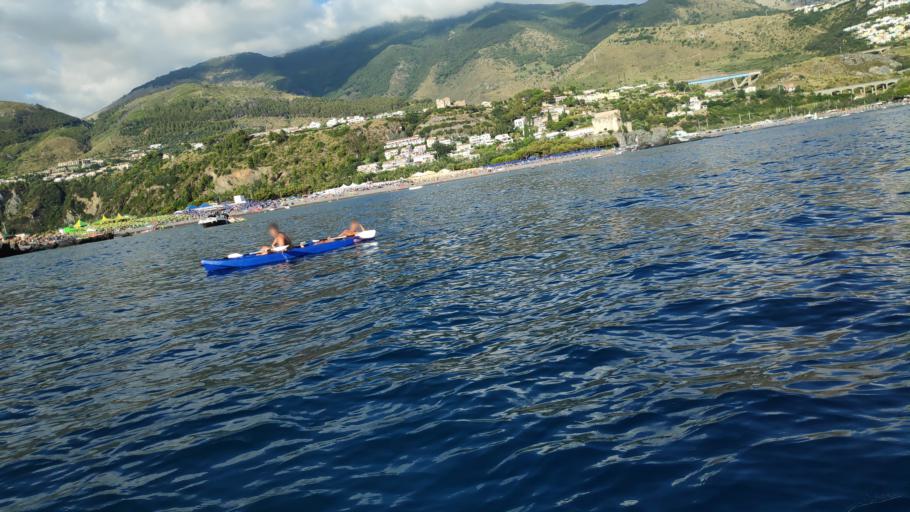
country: IT
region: Calabria
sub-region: Provincia di Cosenza
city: Praia a Mare
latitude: 39.8720
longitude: 15.7809
